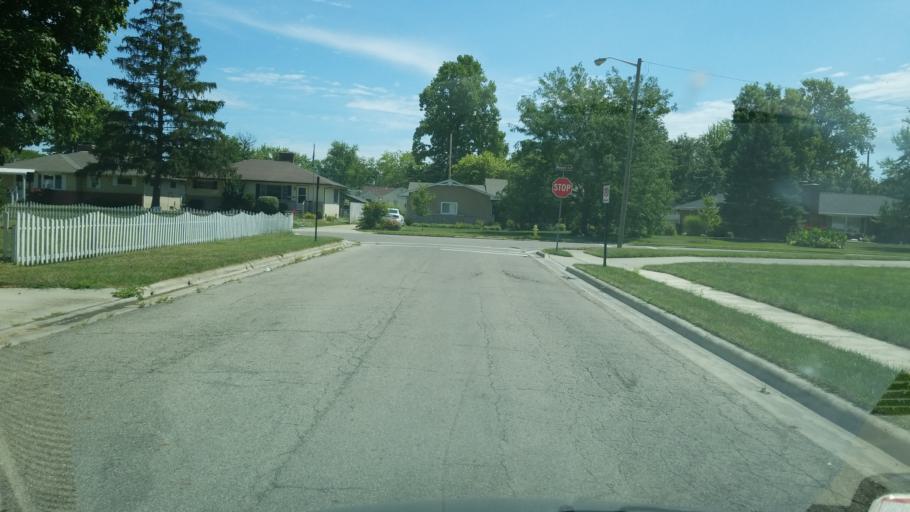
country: US
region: Ohio
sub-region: Franklin County
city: Grove City
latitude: 39.8771
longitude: -83.0909
